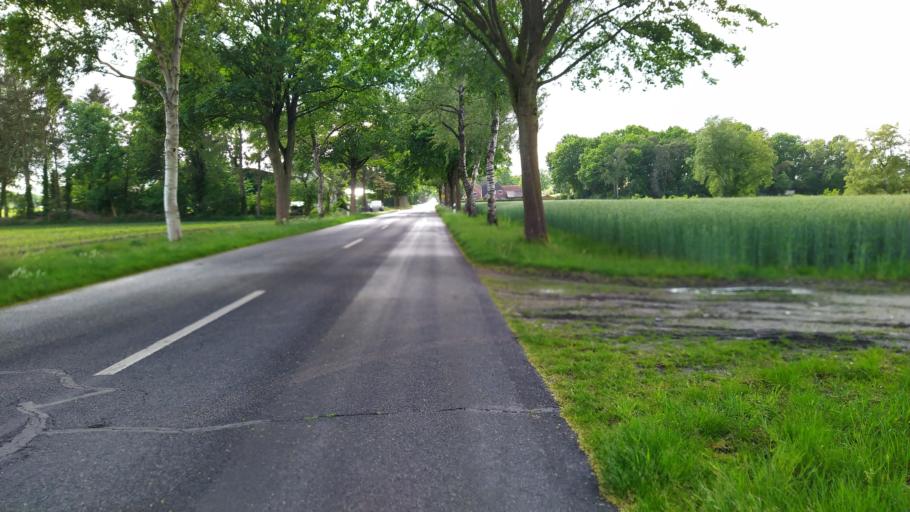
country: DE
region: Lower Saxony
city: Brest
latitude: 53.4522
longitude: 9.3956
